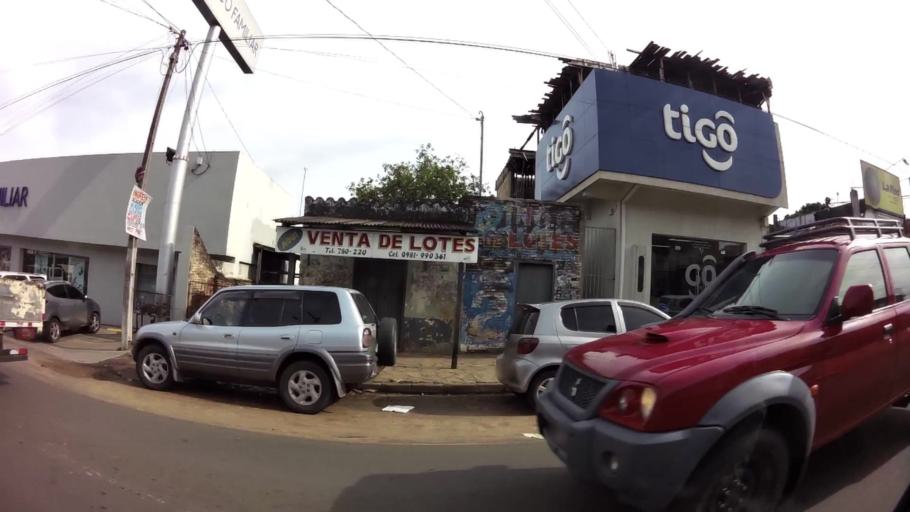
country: PY
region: Central
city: Limpio
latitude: -25.1684
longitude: -57.4744
